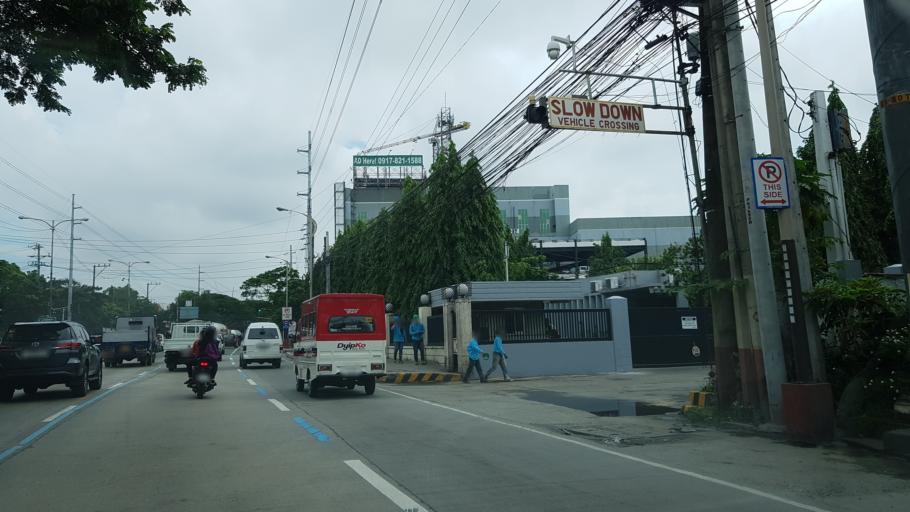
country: PH
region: Metro Manila
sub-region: Pasig
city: Pasig City
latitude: 14.5765
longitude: 121.0730
